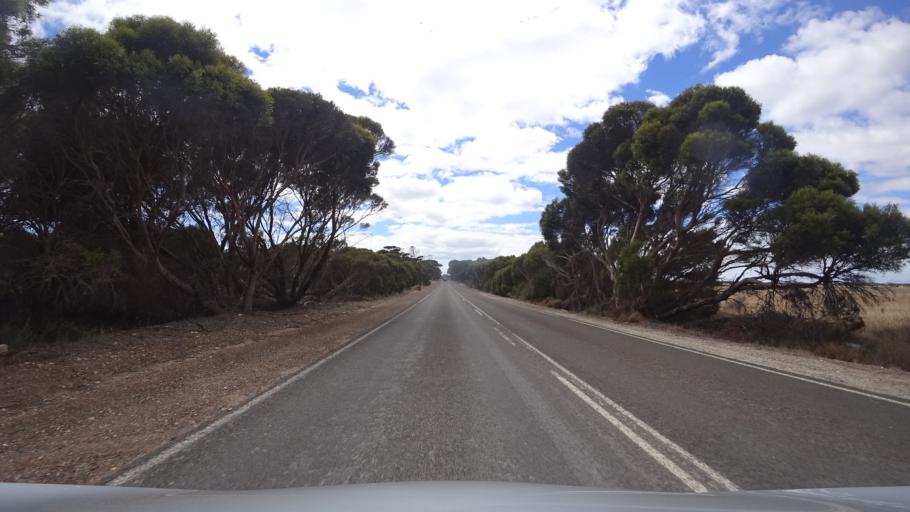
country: AU
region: South Australia
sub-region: Kangaroo Island
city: Kingscote
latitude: -35.6266
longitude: 137.5420
